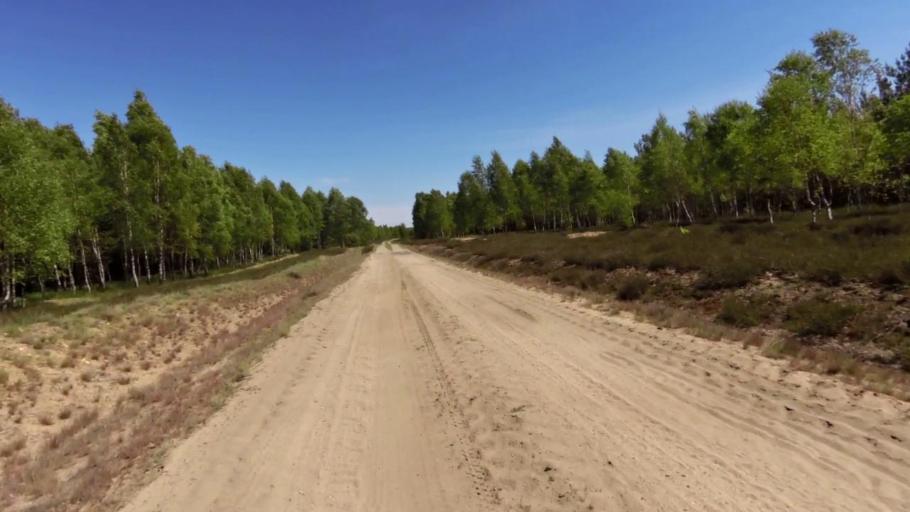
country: PL
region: West Pomeranian Voivodeship
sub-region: Powiat szczecinecki
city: Borne Sulinowo
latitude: 53.5720
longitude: 16.6330
